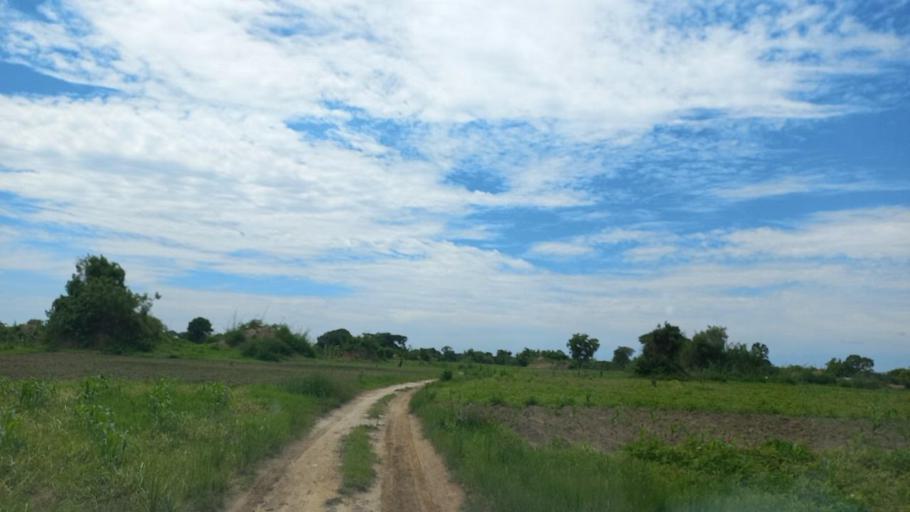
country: ZM
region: Copperbelt
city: Kitwe
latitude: -12.7968
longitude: 28.4014
